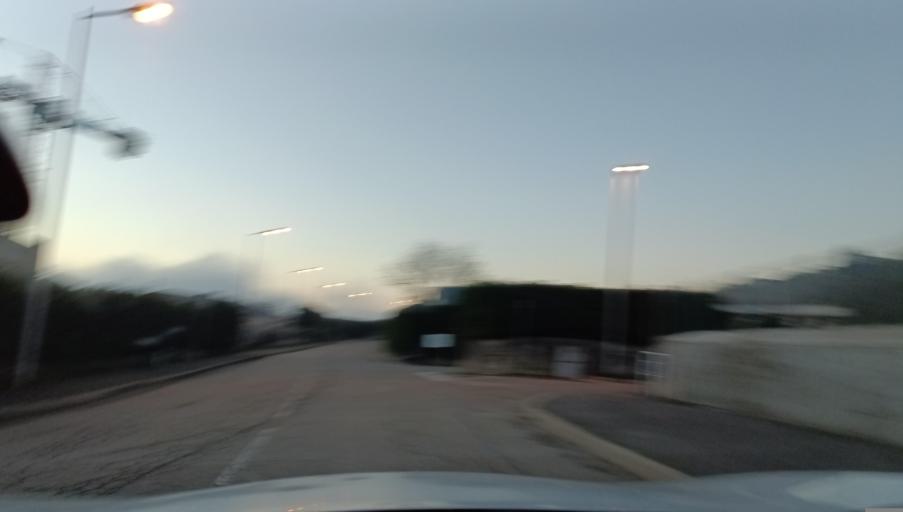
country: FR
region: Rhone-Alpes
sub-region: Departement de l'Isere
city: Chasse-sur-Rhone
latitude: 45.5718
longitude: 4.8175
